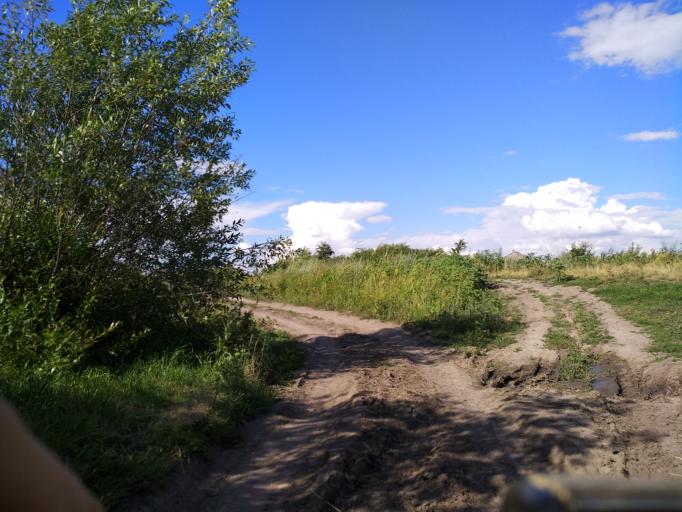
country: RU
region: Lipetsk
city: Dobrinka
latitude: 52.0352
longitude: 40.5622
